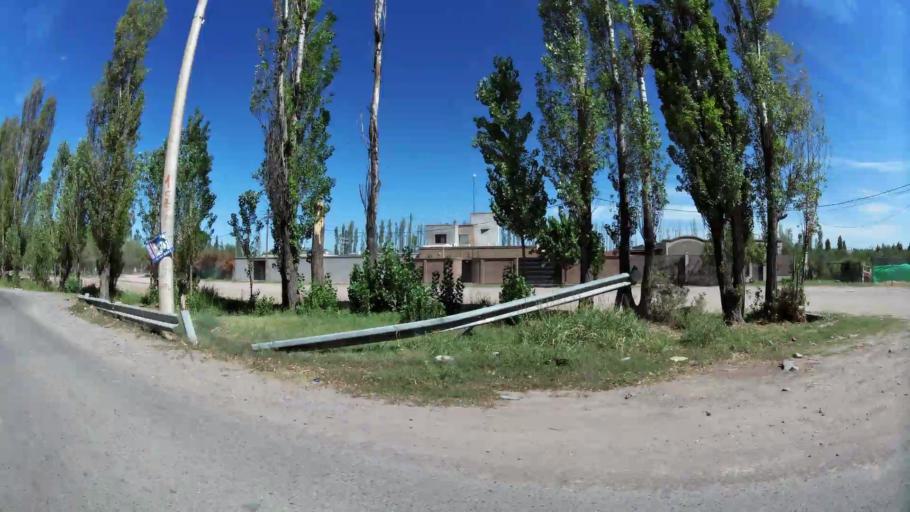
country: AR
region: Mendoza
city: Lujan de Cuyo
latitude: -32.9842
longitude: -68.8514
